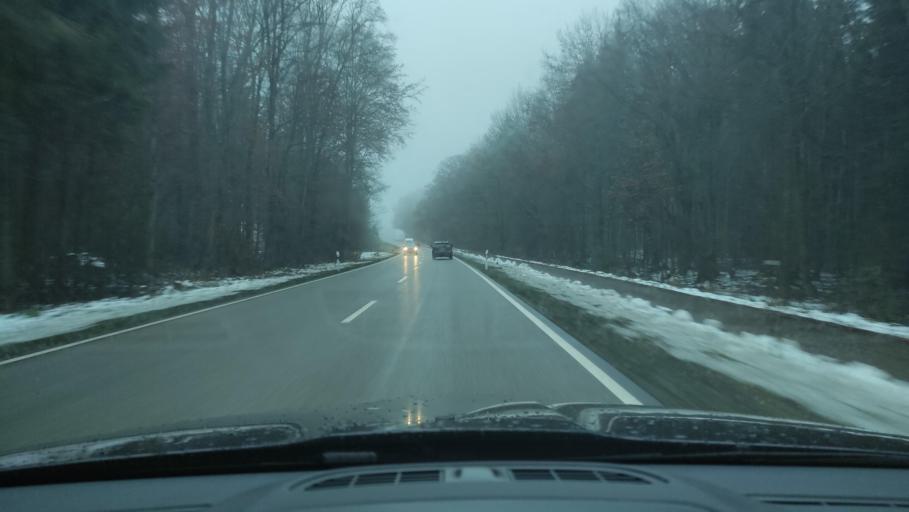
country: DE
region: Bavaria
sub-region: Swabia
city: Weissenhorn
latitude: 48.2927
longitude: 10.1843
